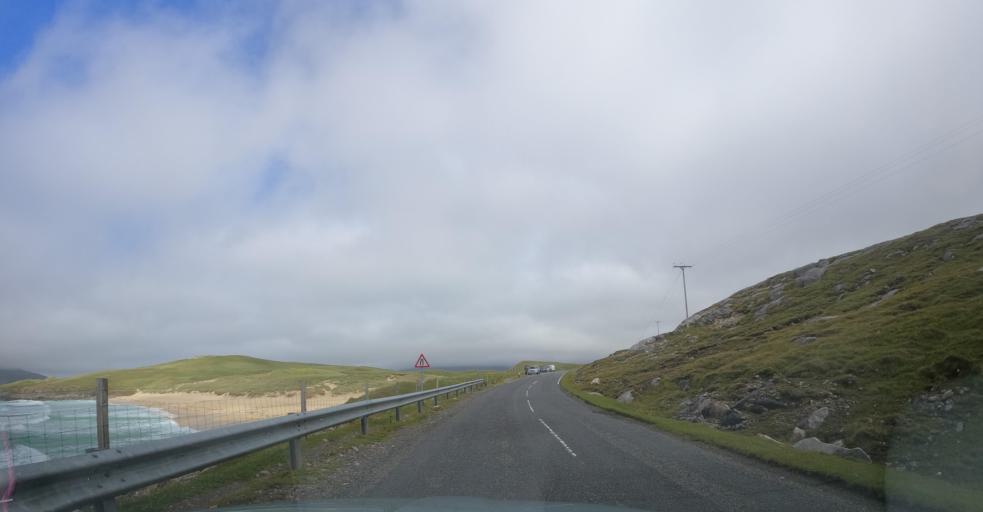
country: GB
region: Scotland
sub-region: Eilean Siar
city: Harris
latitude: 57.8598
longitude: -6.9935
